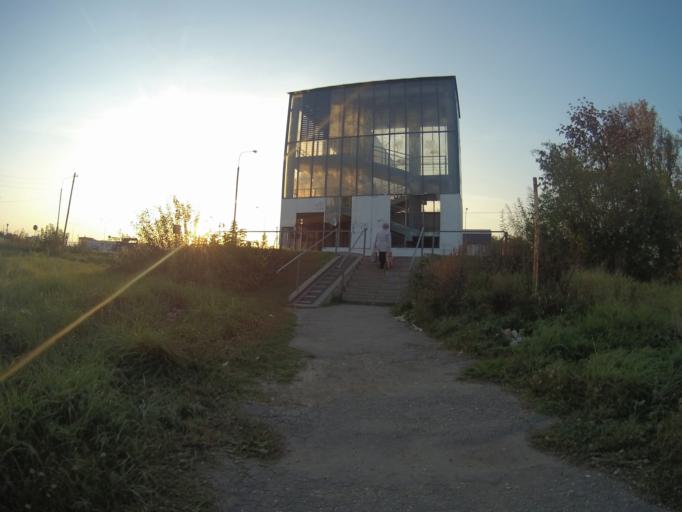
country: RU
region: Vladimir
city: Vladimir
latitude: 56.1166
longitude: 40.3406
